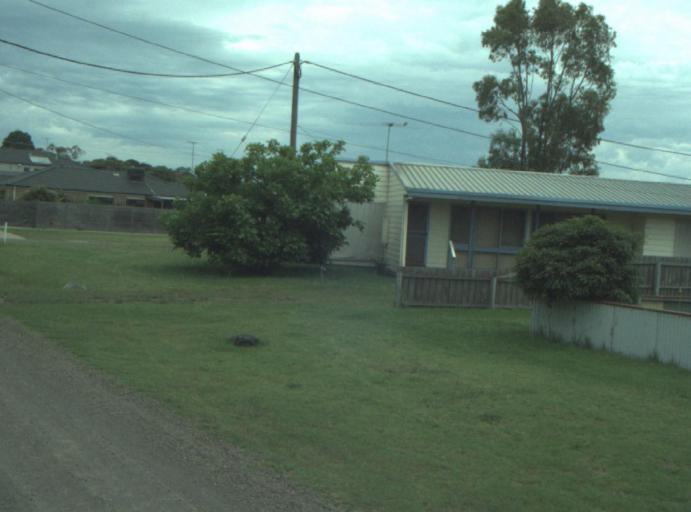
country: AU
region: Victoria
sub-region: Greater Geelong
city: Clifton Springs
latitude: -38.1212
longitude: 144.6689
